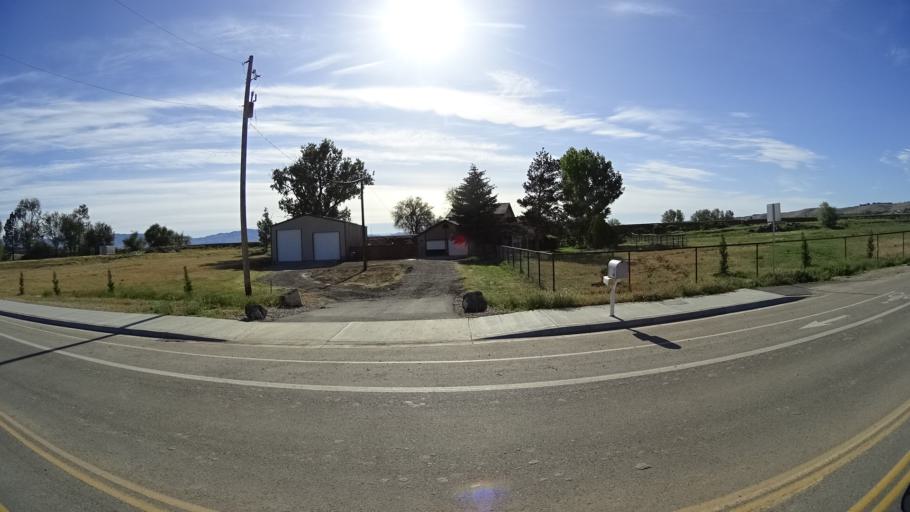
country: US
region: Idaho
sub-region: Ada County
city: Garden City
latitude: 43.5402
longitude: -116.2743
